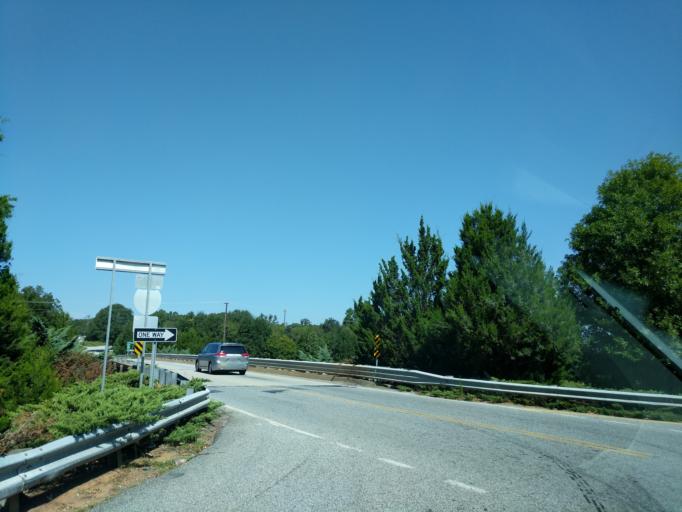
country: US
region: South Carolina
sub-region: Spartanburg County
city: Valley Falls
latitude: 35.0023
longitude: -81.9253
